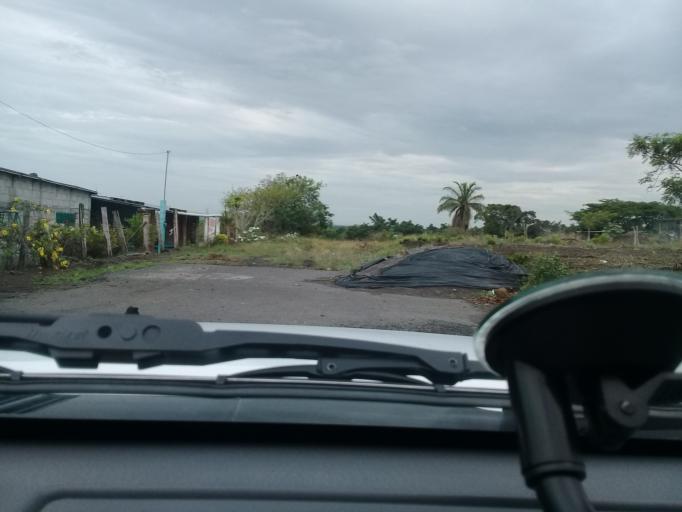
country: MX
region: Veracruz
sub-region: Puente Nacional
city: Cabezas
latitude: 19.3337
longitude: -96.3873
